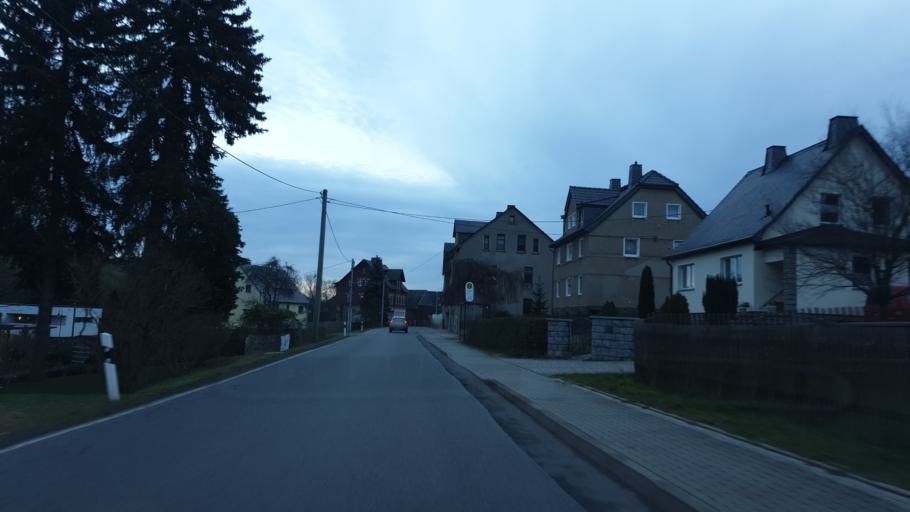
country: DE
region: Saxony
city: Hartenstein
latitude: 50.6904
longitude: 12.6708
